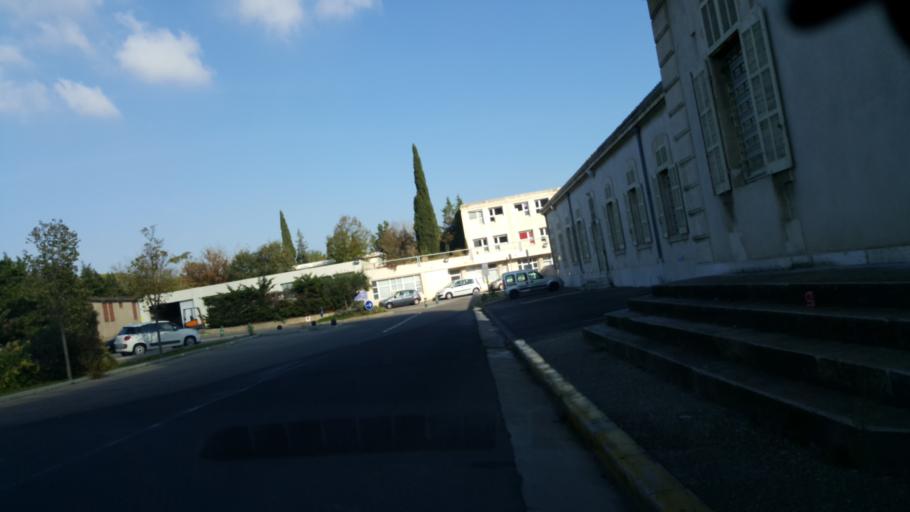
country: FR
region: Provence-Alpes-Cote d'Azur
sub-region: Departement des Bouches-du-Rhone
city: Marseille 09
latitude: 43.2604
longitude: 5.4107
